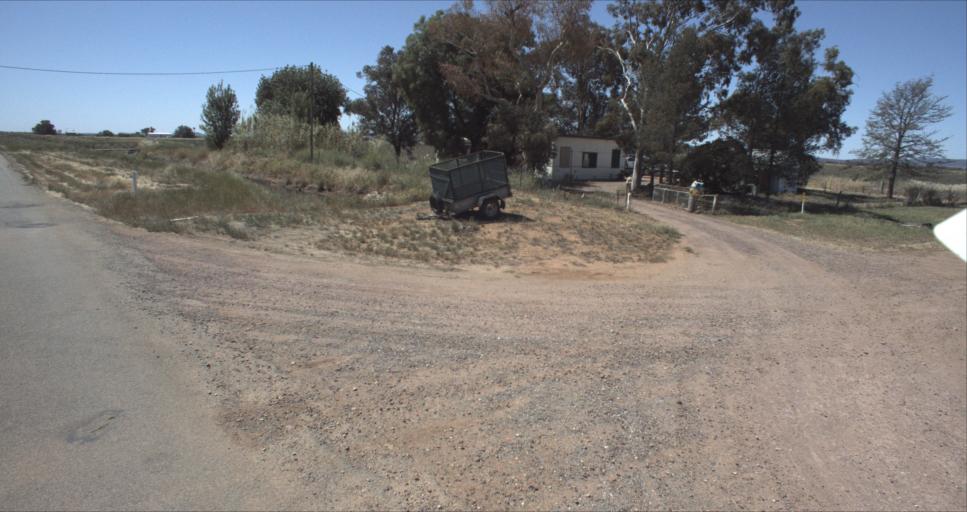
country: AU
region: New South Wales
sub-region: Leeton
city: Leeton
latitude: -34.5115
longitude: 146.3449
